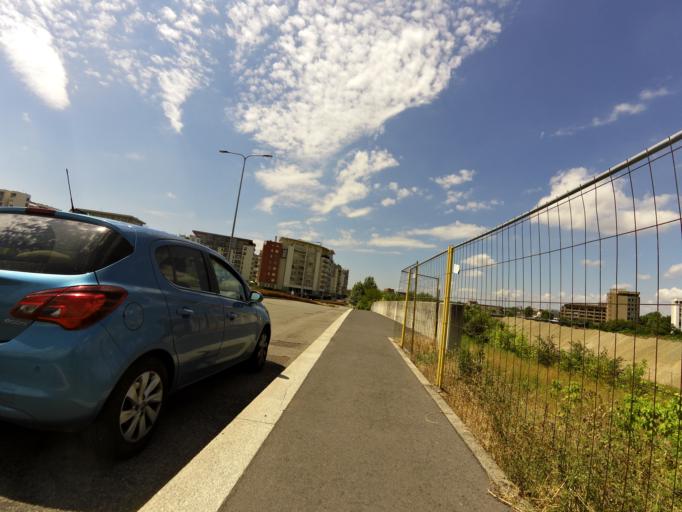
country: IT
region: Lombardy
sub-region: Citta metropolitana di Milano
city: Chiaravalle
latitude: 45.4404
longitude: 9.2436
